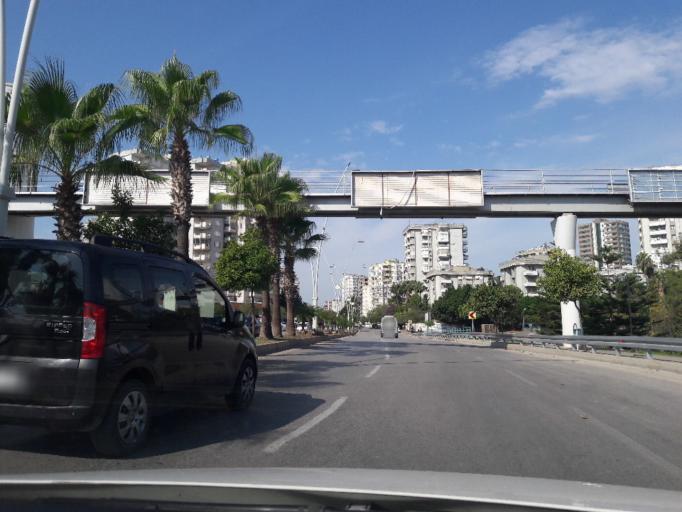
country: TR
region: Adana
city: Adana
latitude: 37.0144
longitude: 35.3270
